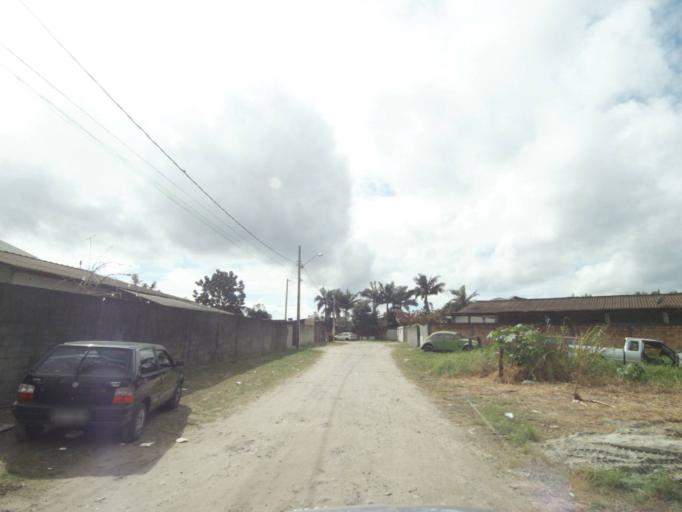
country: BR
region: Parana
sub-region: Paranagua
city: Paranagua
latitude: -25.5719
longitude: -48.5628
